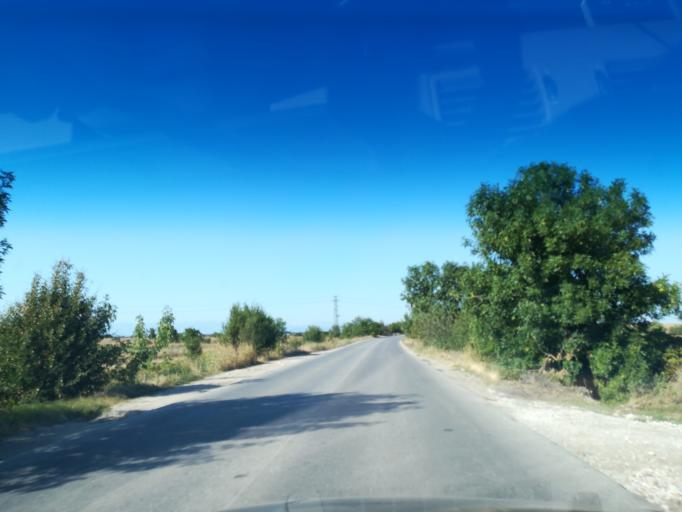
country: BG
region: Plovdiv
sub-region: Obshtina Plovdiv
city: Plovdiv
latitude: 42.1700
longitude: 24.8142
